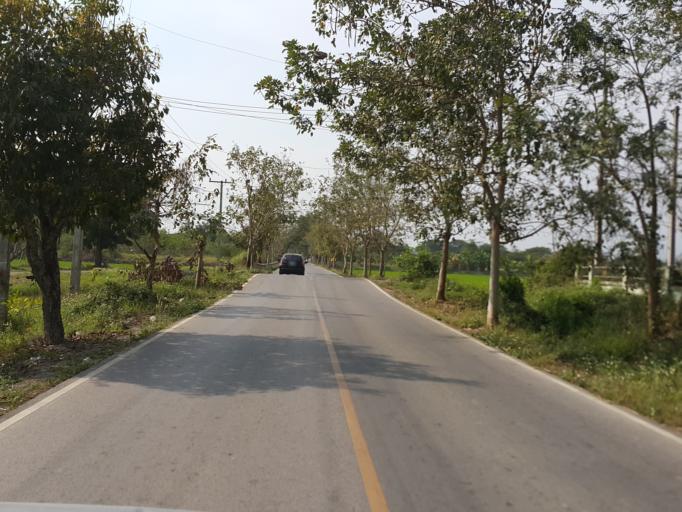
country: TH
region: Chiang Mai
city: Hang Dong
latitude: 18.6822
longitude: 98.9783
